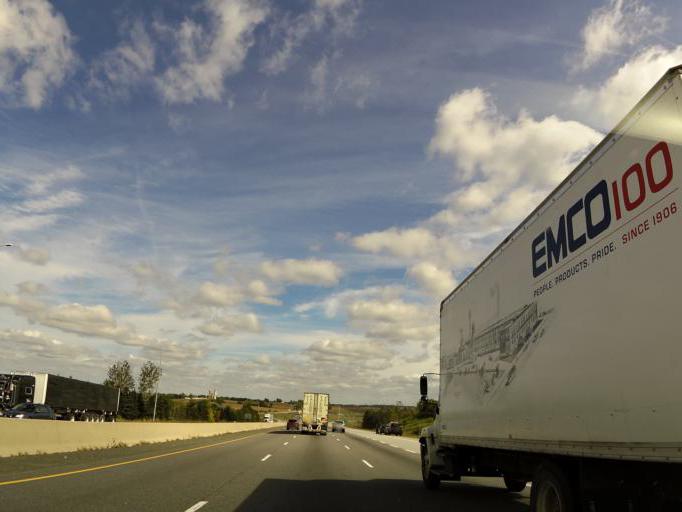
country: CA
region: Ontario
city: Ingersoll
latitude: 42.9744
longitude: -80.9600
